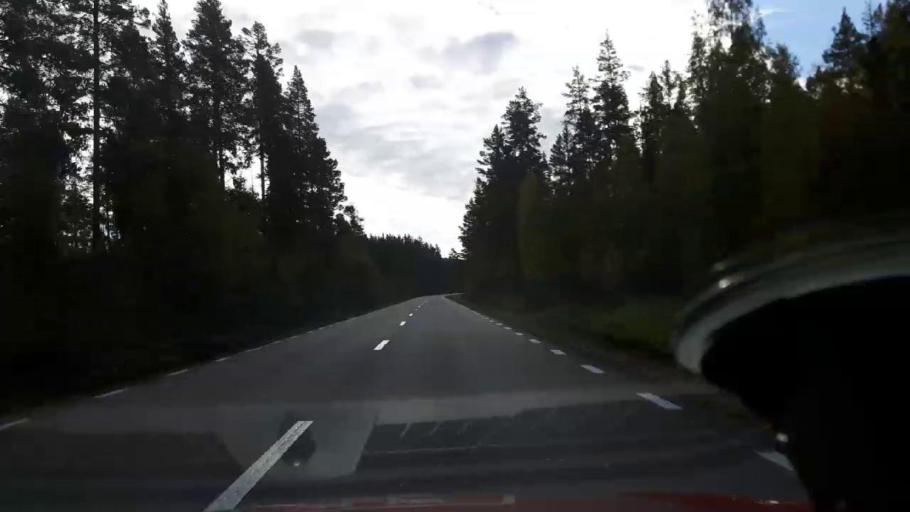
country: SE
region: Gaevleborg
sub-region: Ljusdals Kommun
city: Farila
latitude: 62.0187
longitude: 15.2349
